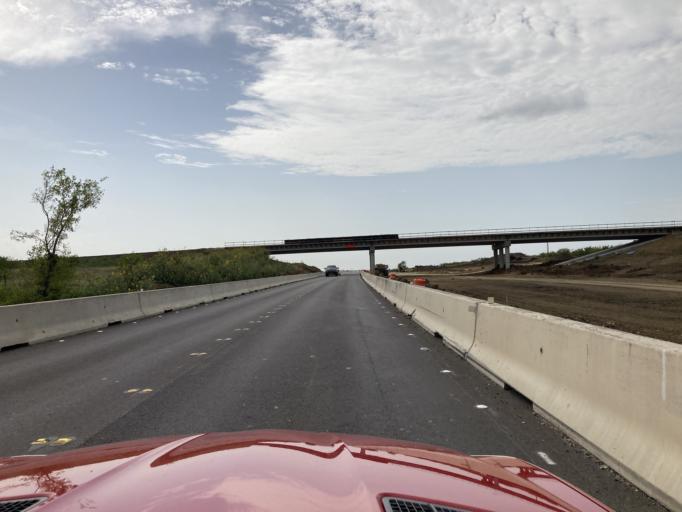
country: US
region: Texas
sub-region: Navarro County
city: Corsicana
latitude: 32.0484
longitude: -96.4187
